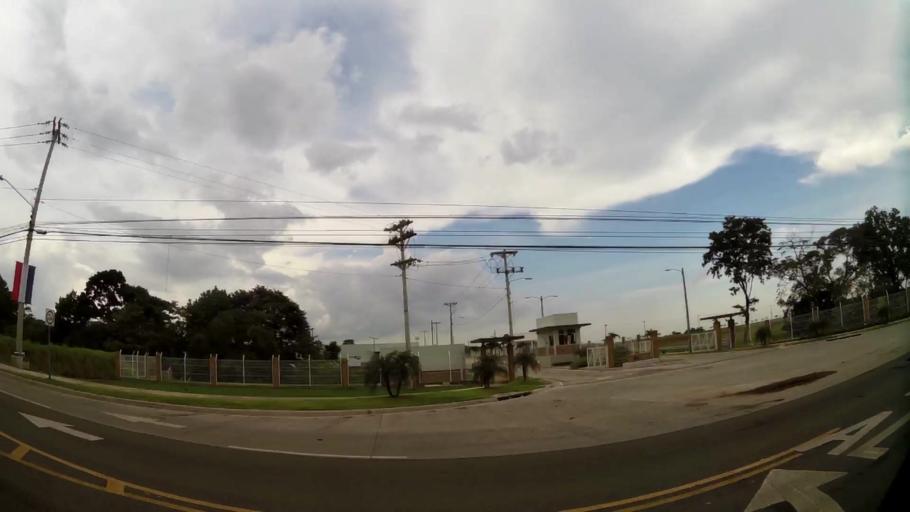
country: PA
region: Panama
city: Cabra Numero Uno
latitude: 9.1097
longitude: -79.3590
